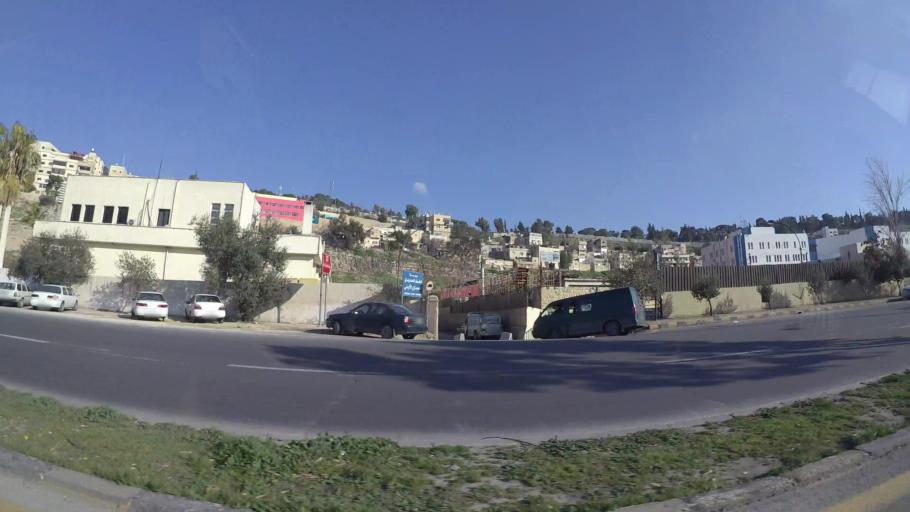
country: JO
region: Amman
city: Amman
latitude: 31.9716
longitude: 35.9706
